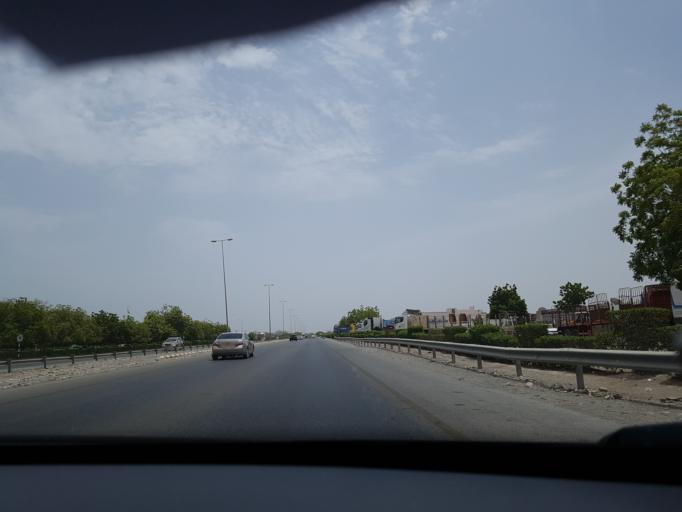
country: OM
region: Muhafazat Masqat
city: As Sib al Jadidah
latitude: 23.6915
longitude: 58.0476
